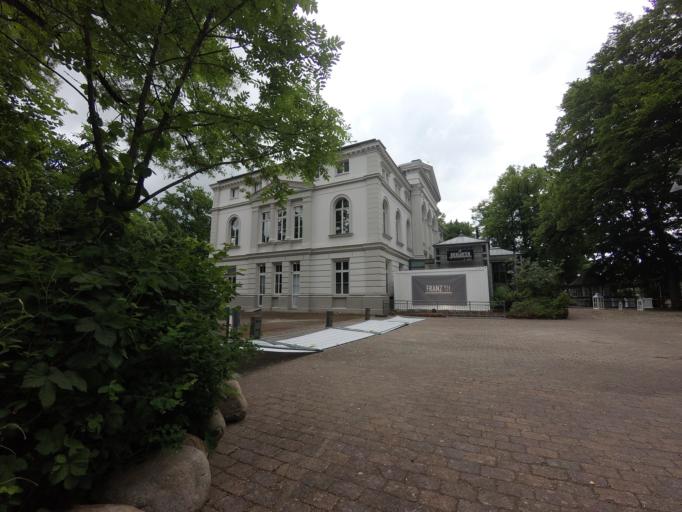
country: DE
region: Lower Saxony
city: Celle
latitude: 52.6194
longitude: 10.0824
